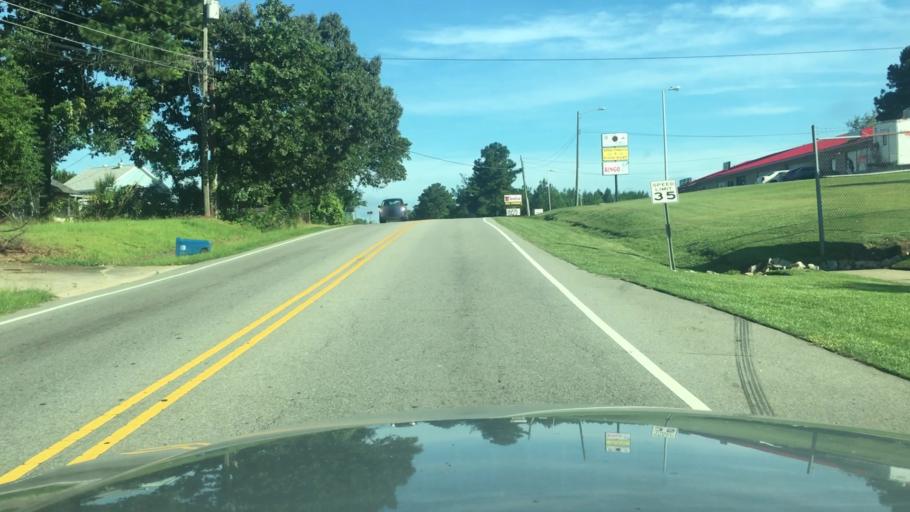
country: US
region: North Carolina
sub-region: Cumberland County
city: Fayetteville
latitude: 35.1216
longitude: -78.8853
